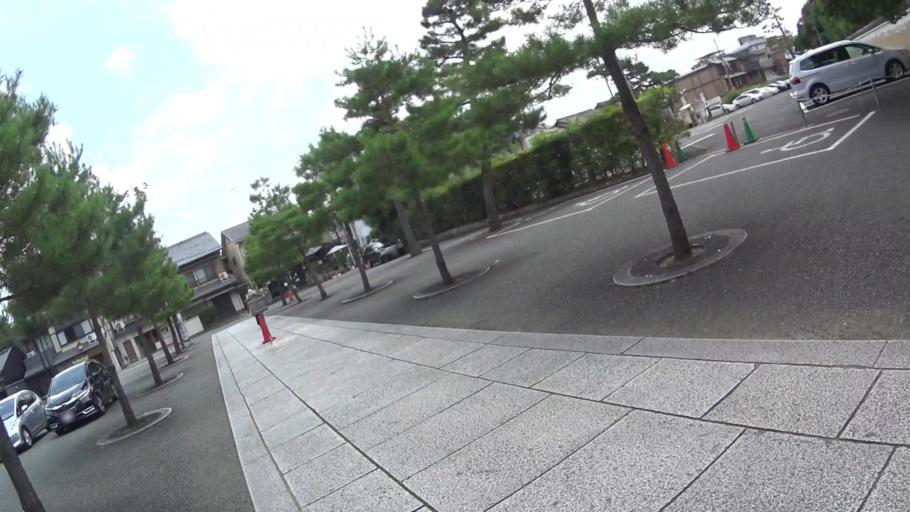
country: JP
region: Kyoto
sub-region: Kyoto-shi
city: Kamigyo-ku
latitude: 35.0485
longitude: 135.7492
